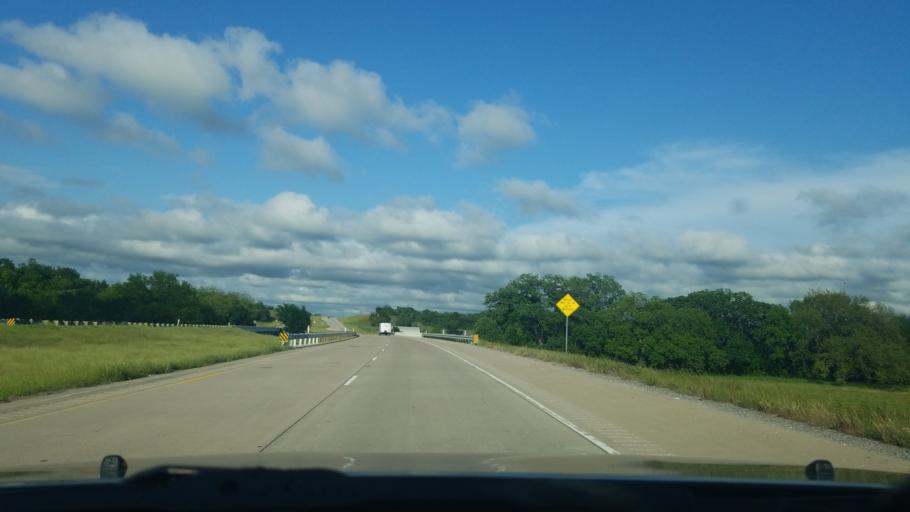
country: US
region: Texas
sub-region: Wise County
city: Decatur
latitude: 33.2458
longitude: -97.4489
